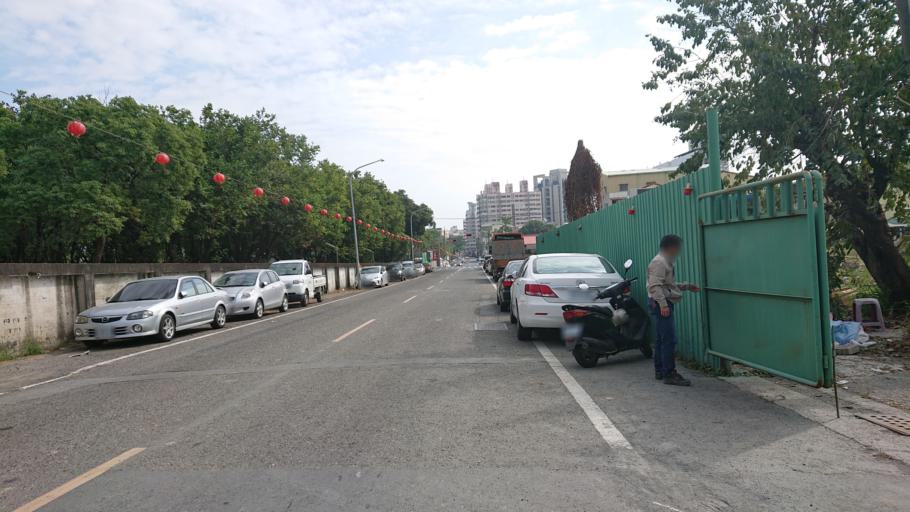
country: TW
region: Taiwan
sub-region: Tainan
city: Tainan
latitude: 23.0206
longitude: 120.2539
